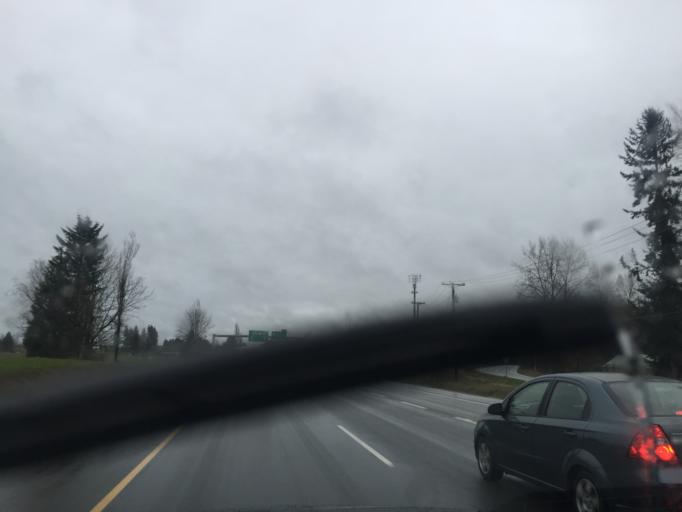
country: CA
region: British Columbia
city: Aldergrove
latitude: 49.1037
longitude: -122.4986
